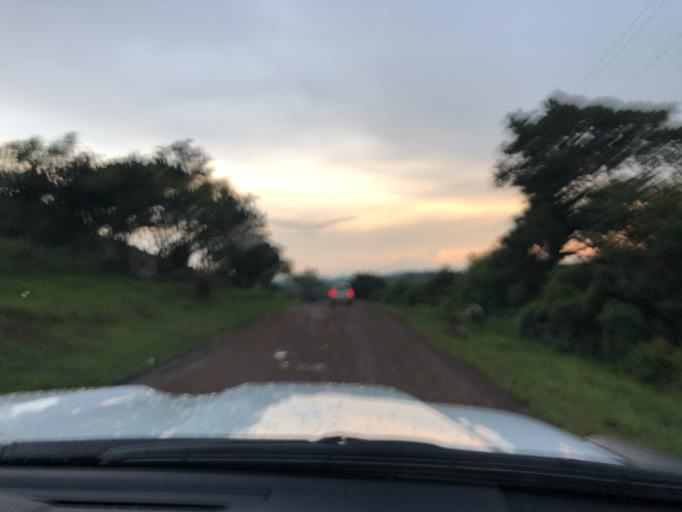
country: NI
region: Chontales
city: La Libertad
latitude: 12.1722
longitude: -85.1772
